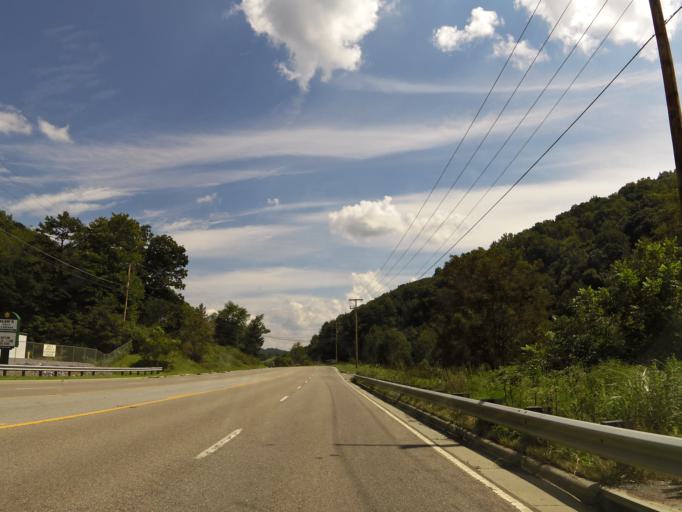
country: US
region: Virginia
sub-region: Washington County
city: Abingdon
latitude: 36.7079
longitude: -81.9233
